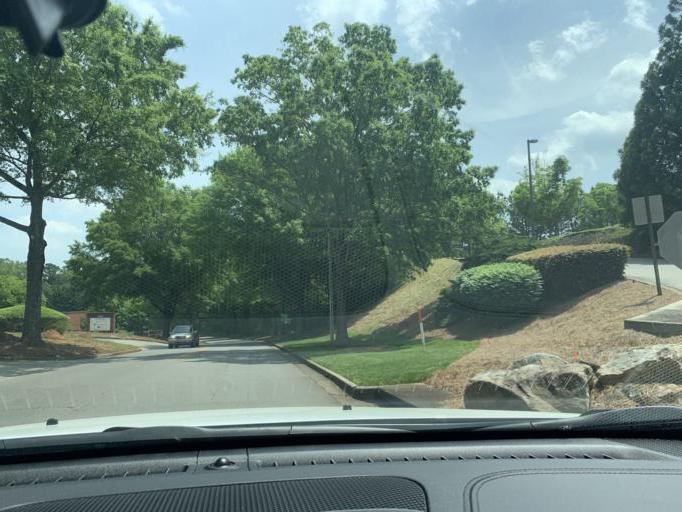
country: US
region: Georgia
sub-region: Fulton County
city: Johns Creek
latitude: 34.1210
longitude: -84.2020
